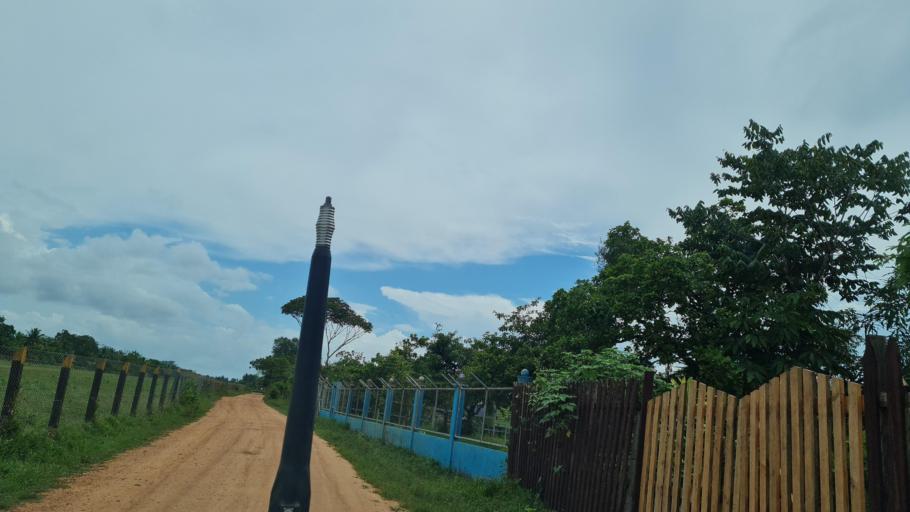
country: NI
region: Atlantico Norte (RAAN)
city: Waspam
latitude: 14.7449
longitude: -83.9658
